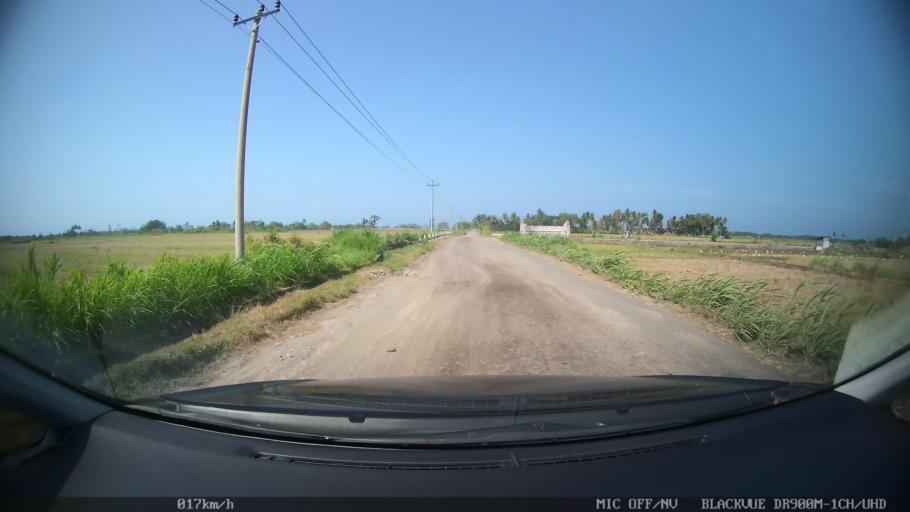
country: ID
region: Daerah Istimewa Yogyakarta
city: Srandakan
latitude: -7.9713
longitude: 110.2109
